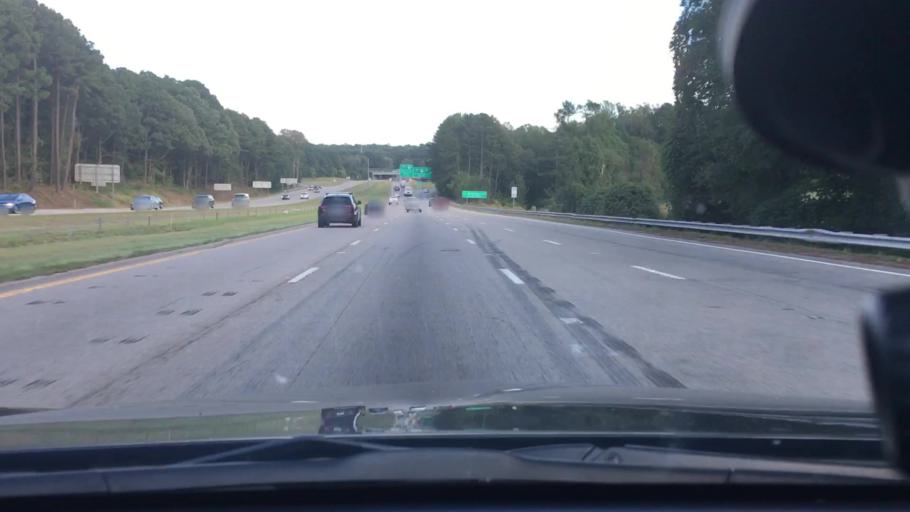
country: US
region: North Carolina
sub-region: Wake County
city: West Raleigh
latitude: 35.8037
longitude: -78.7027
